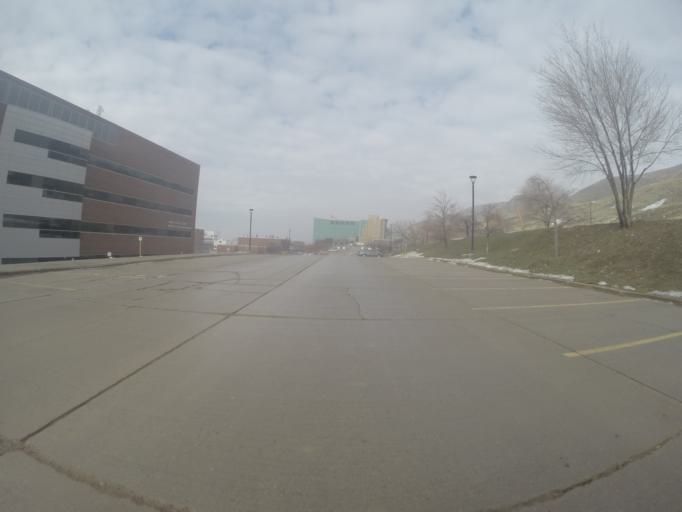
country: US
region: Utah
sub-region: Salt Lake County
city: Salt Lake City
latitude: 40.7699
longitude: -111.8317
